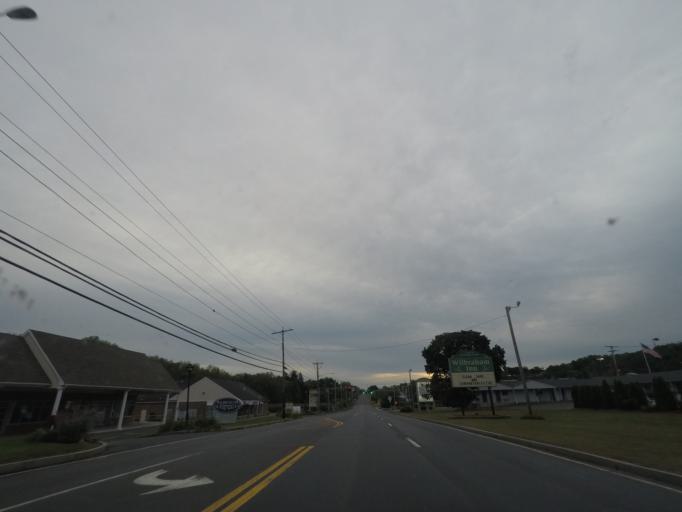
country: US
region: Massachusetts
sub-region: Hampden County
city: Ludlow
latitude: 42.1496
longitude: -72.4737
